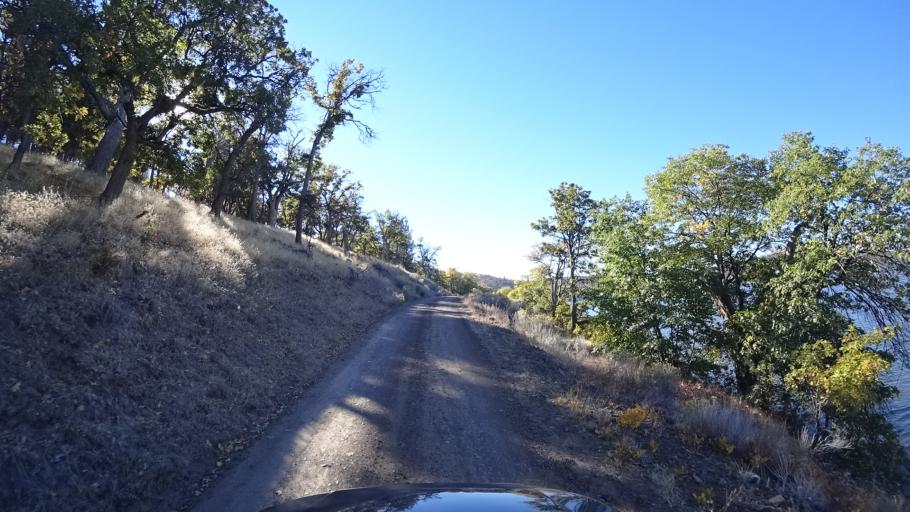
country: US
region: California
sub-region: Siskiyou County
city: Montague
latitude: 41.9913
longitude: -122.3105
